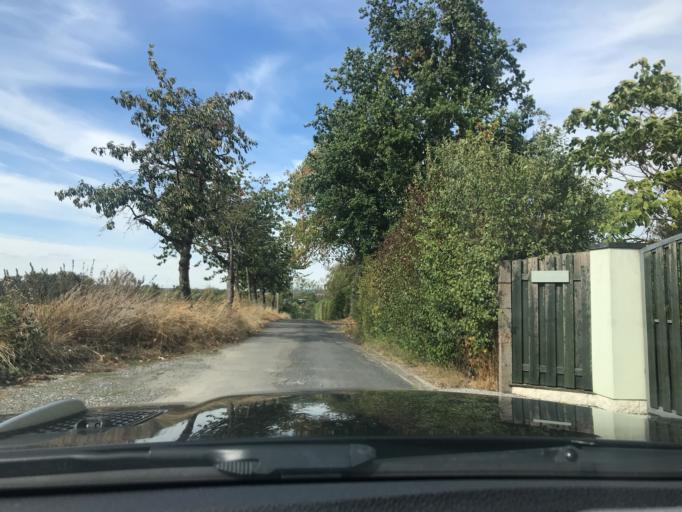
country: DE
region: Thuringia
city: Muehlhausen
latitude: 51.2158
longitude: 10.4332
